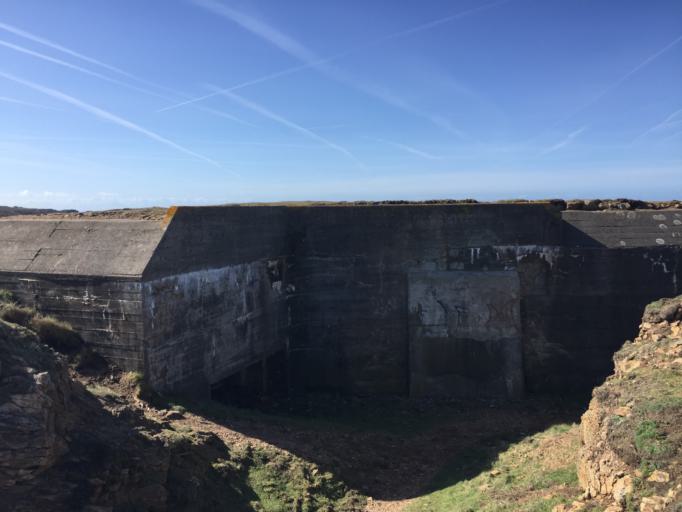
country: JE
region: St Helier
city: Saint Helier
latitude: 49.2522
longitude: -2.2521
